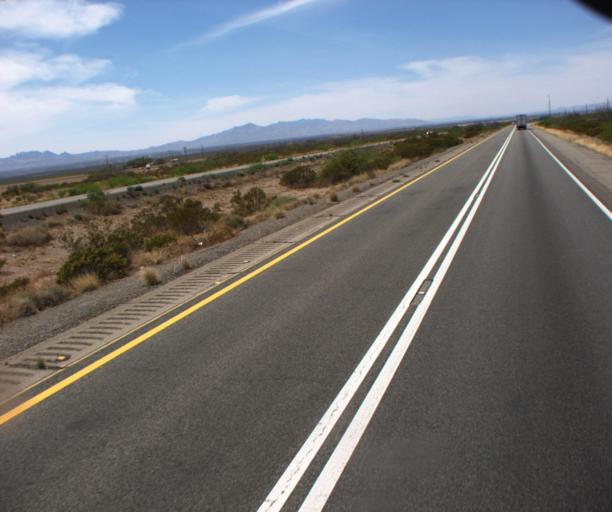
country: US
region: New Mexico
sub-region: Hidalgo County
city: Lordsburg
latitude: 32.2522
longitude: -109.1554
